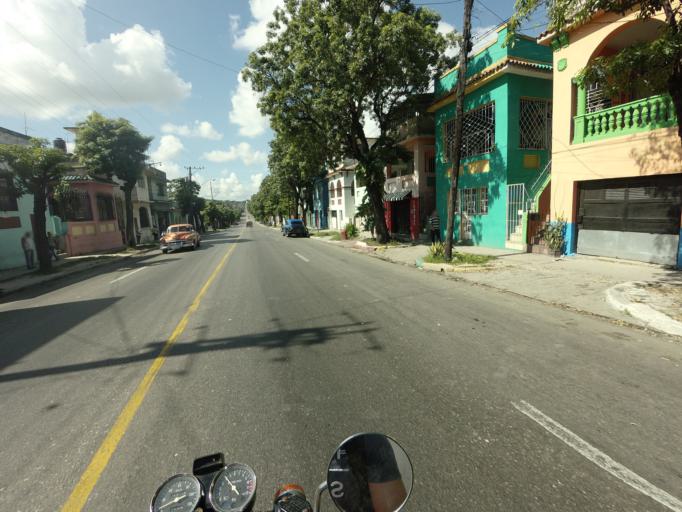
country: TM
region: Balkan
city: Gumdag
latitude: 38.8433
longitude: 54.1816
